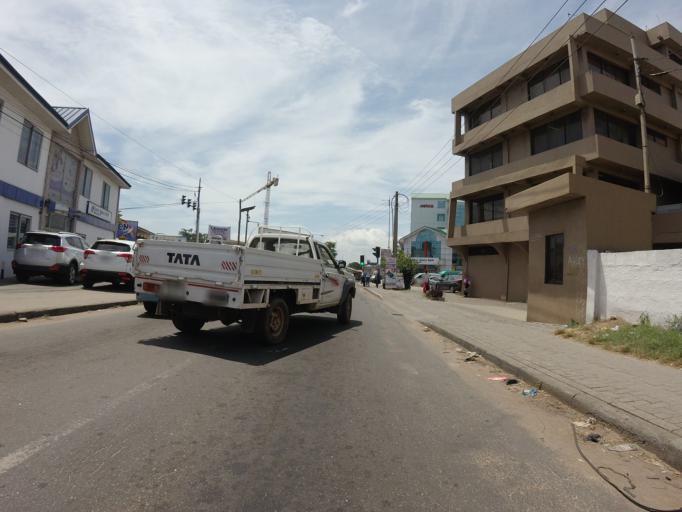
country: GH
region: Greater Accra
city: Accra
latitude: 5.5563
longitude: -0.2116
